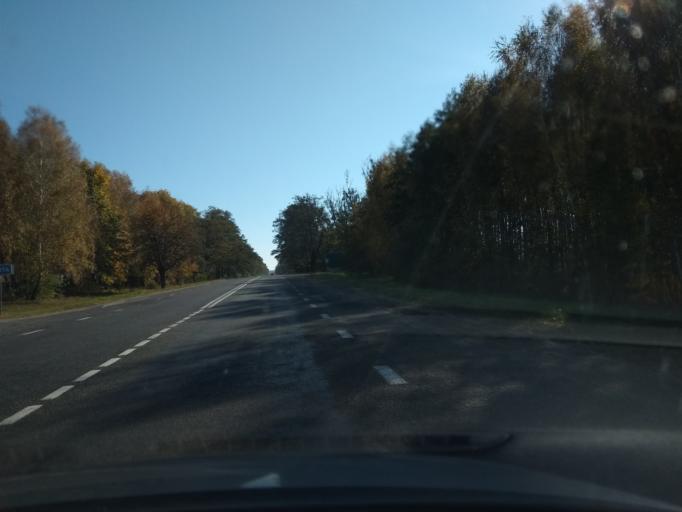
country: BY
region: Brest
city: Malaryta
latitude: 51.9338
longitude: 24.0522
